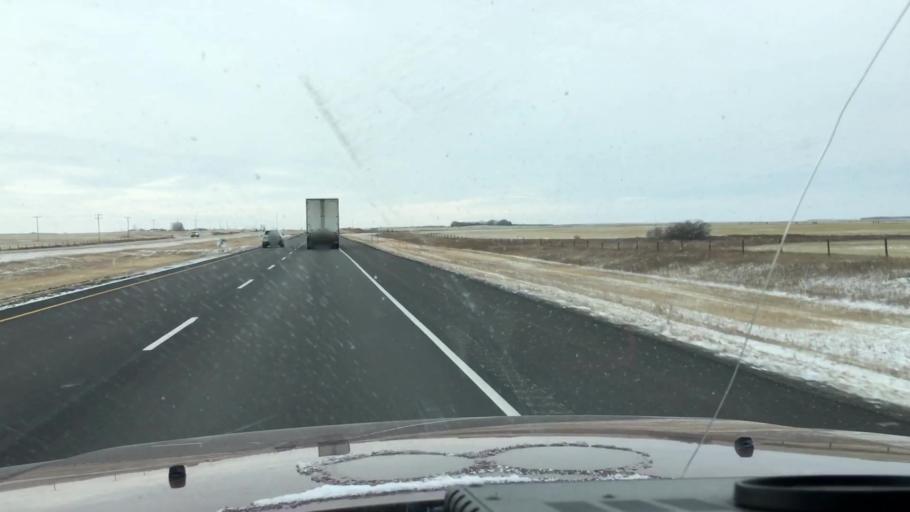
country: CA
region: Saskatchewan
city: Saskatoon
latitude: 51.7976
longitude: -106.4880
